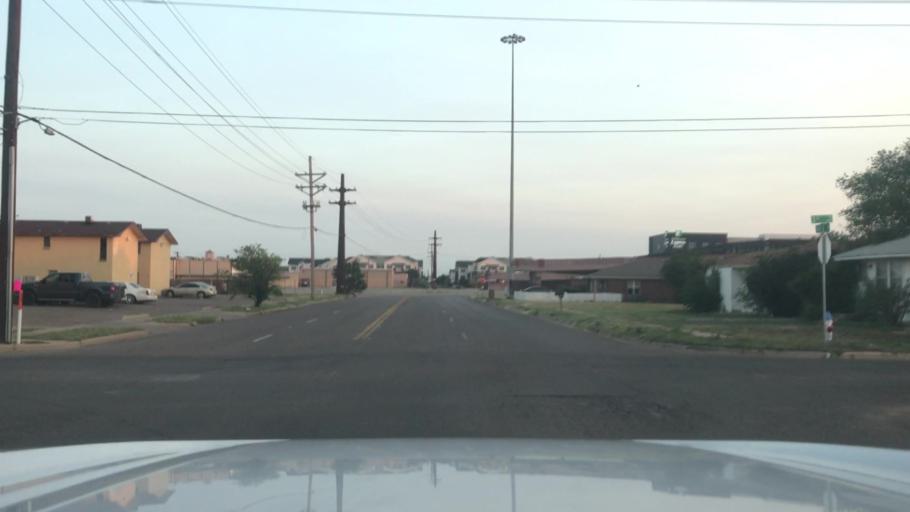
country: US
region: Texas
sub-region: Lubbock County
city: Lubbock
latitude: 33.5944
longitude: -101.8619
